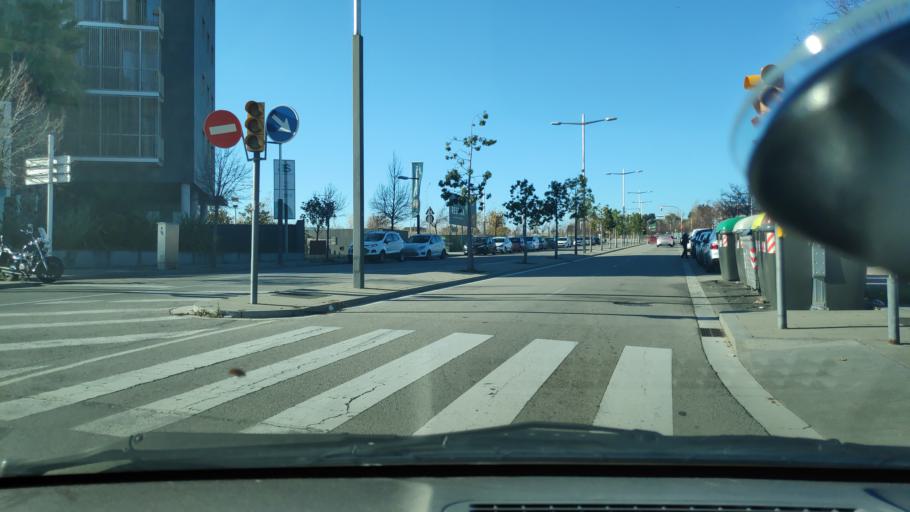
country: ES
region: Catalonia
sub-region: Provincia de Barcelona
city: Sant Quirze del Valles
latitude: 41.5401
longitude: 2.0898
